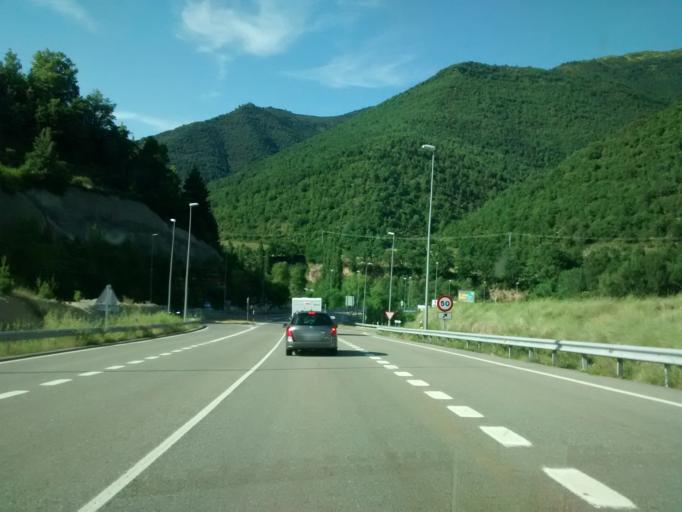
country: ES
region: Aragon
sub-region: Provincia de Huesca
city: Fiscal
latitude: 42.4990
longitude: -0.1209
